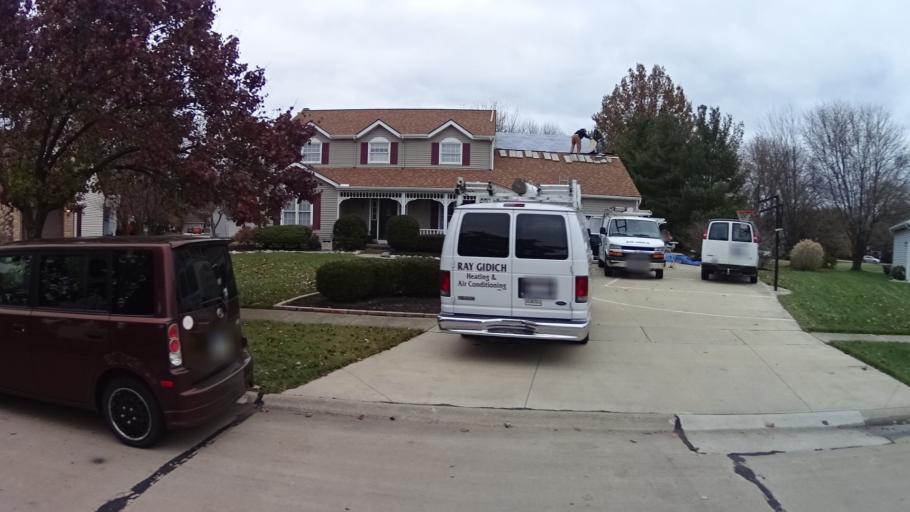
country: US
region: Ohio
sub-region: Lorain County
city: Avon Center
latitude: 41.4886
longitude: -81.9899
